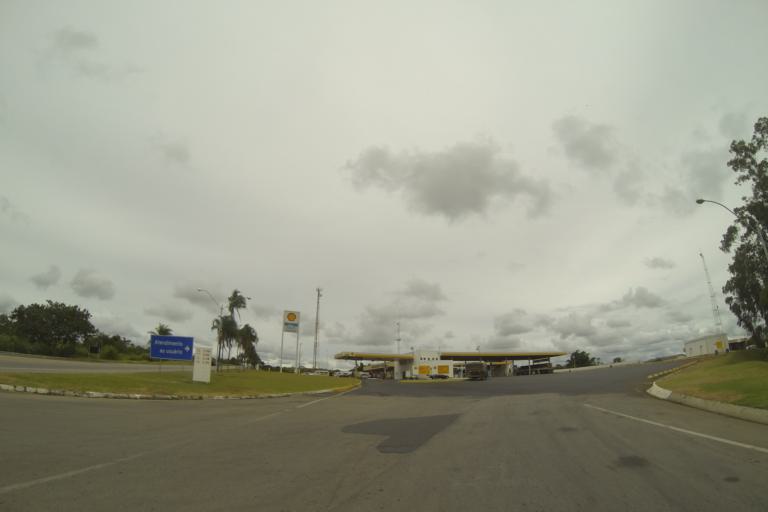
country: BR
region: Minas Gerais
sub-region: Ibia
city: Ibia
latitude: -19.5911
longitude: -46.4941
